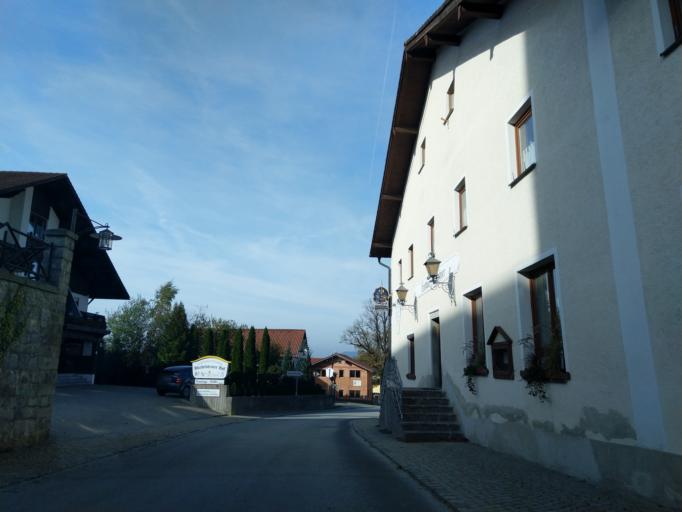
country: DE
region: Bavaria
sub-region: Lower Bavaria
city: Grattersdorf
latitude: 48.8039
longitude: 13.1524
